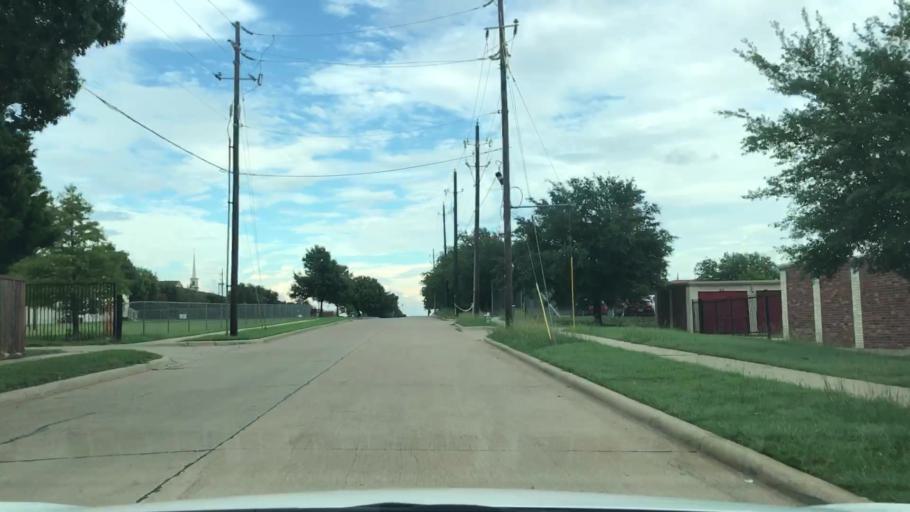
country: US
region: Texas
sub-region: Collin County
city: Frisco
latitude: 33.1408
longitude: -96.8075
